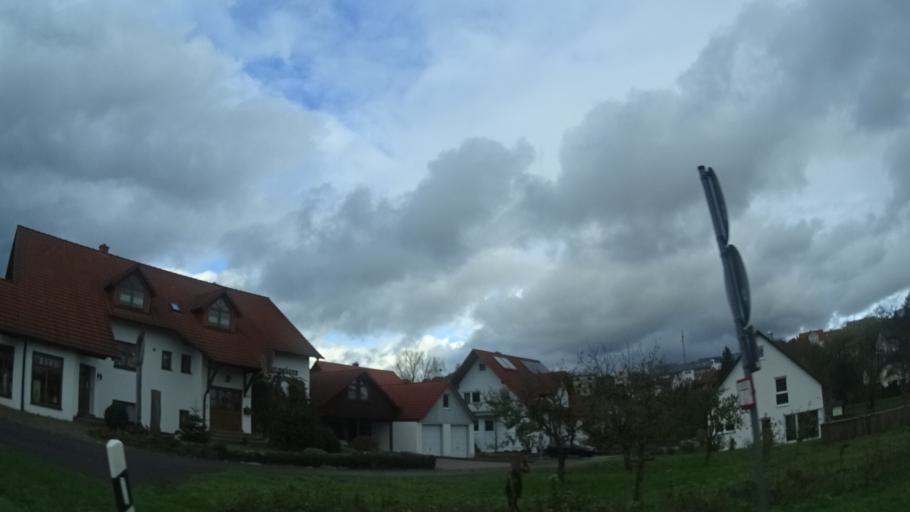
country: DE
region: Bavaria
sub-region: Regierungsbezirk Unterfranken
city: Hohenroth
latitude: 50.3263
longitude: 10.1655
